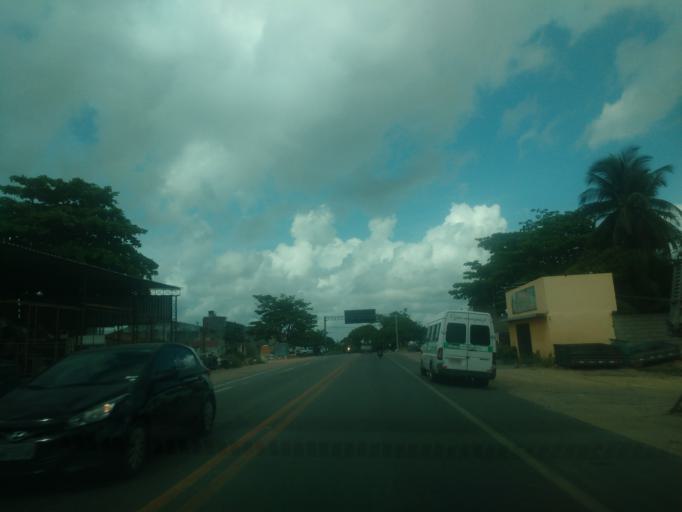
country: BR
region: Alagoas
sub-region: Satuba
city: Satuba
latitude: -9.5659
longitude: -35.7912
